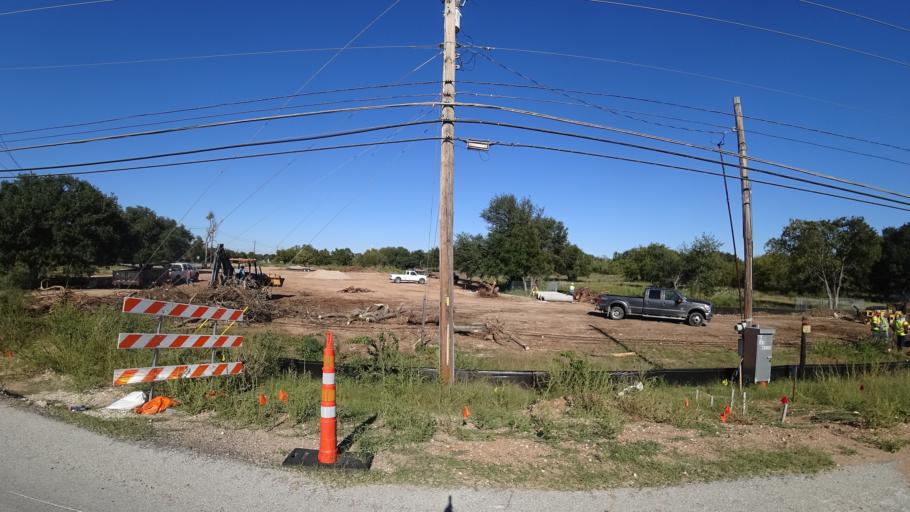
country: US
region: Texas
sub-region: Travis County
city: Hornsby Bend
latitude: 30.2765
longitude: -97.6369
